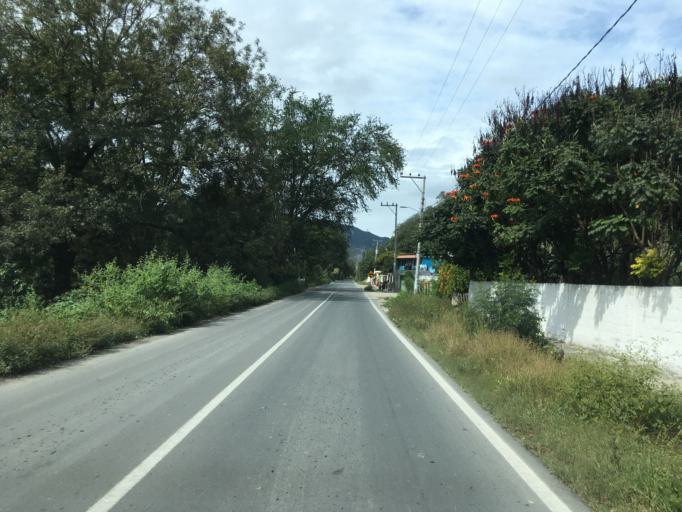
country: MX
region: Hidalgo
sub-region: San Agustin Metzquititlan
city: Mezquititlan
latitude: 20.5056
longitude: -98.7013
